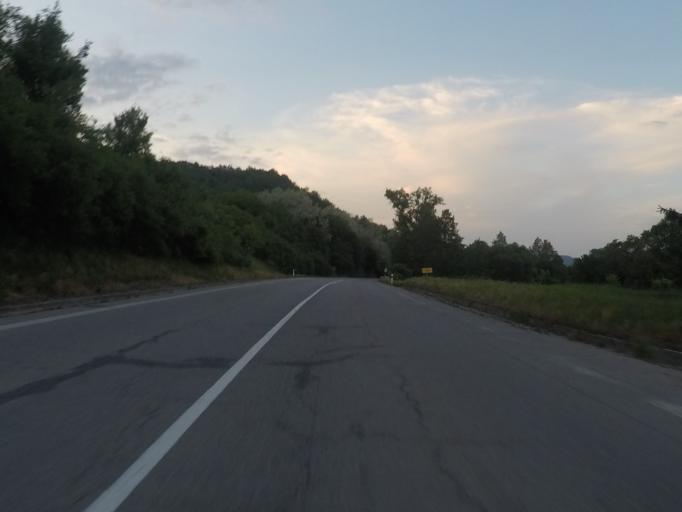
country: SK
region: Banskobystricky
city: Rimavska Sobota
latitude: 48.5142
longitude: 19.9424
